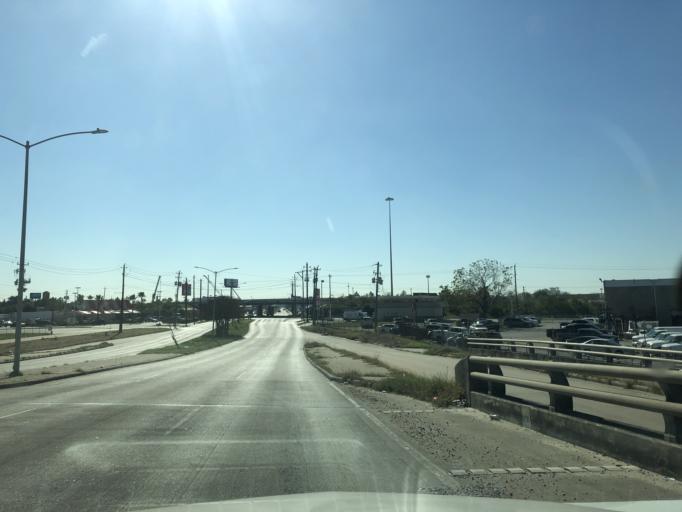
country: US
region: Texas
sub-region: Harris County
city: Houston
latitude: 29.8099
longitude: -95.3020
